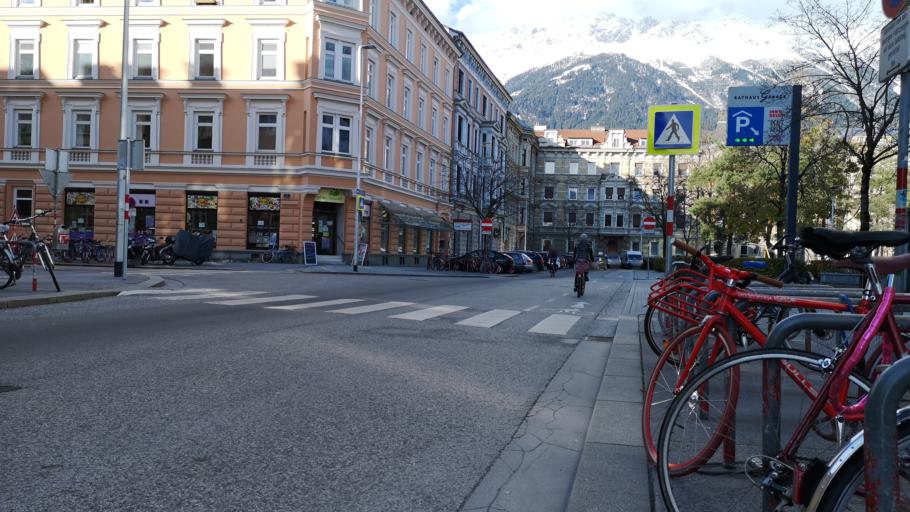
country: AT
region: Tyrol
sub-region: Innsbruck Stadt
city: Innsbruck
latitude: 47.2654
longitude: 11.3916
